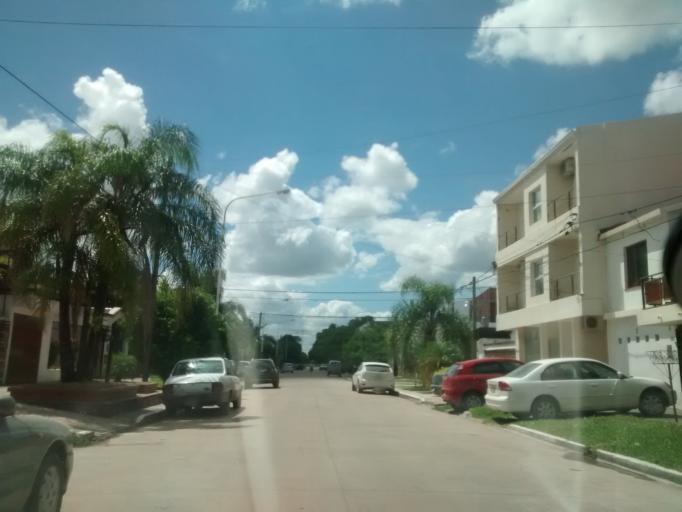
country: AR
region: Chaco
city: Resistencia
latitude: -27.4531
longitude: -59.0010
